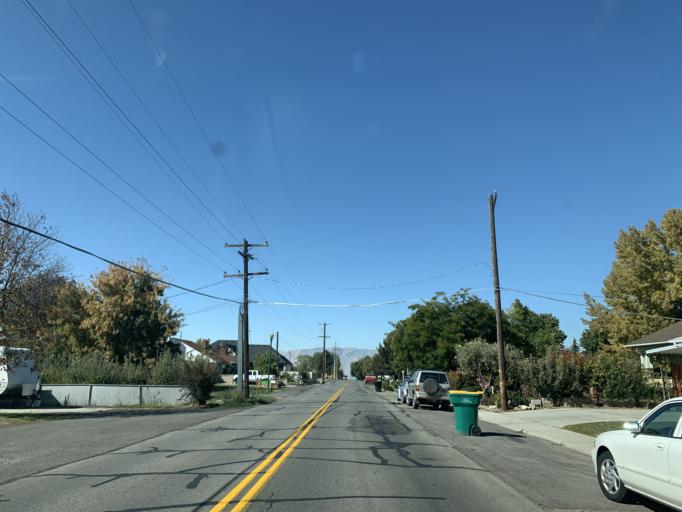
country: US
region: Utah
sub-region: Utah County
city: Orem
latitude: 40.2607
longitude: -111.6892
